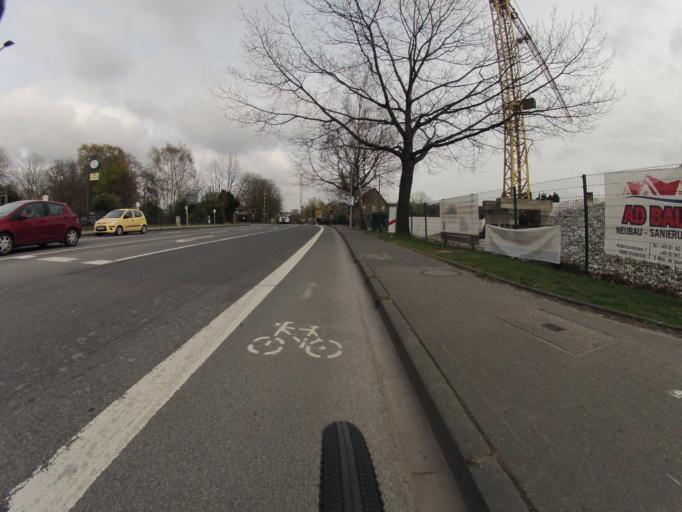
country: DE
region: North Rhine-Westphalia
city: Ibbenburen
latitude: 52.2898
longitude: 7.7212
